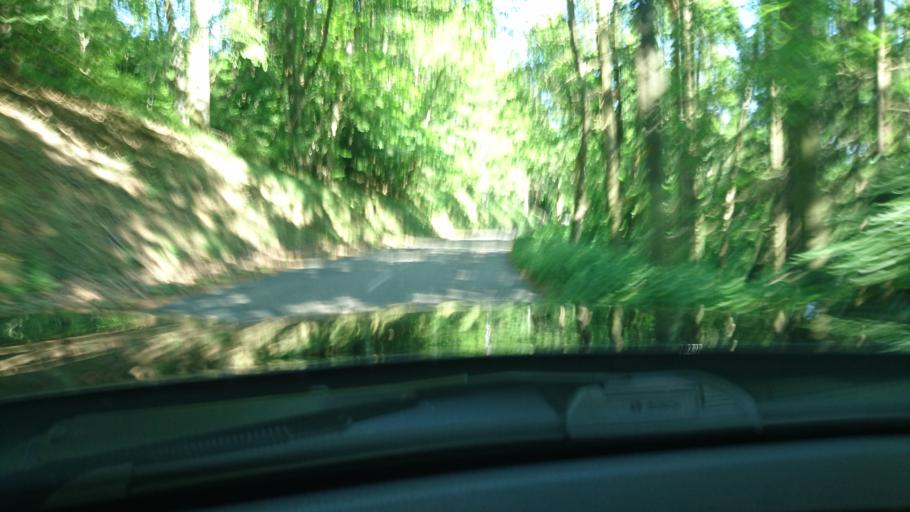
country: FR
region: Rhone-Alpes
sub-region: Departement du Rhone
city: Saint-Pierre-la-Palud
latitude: 45.7652
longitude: 4.6024
